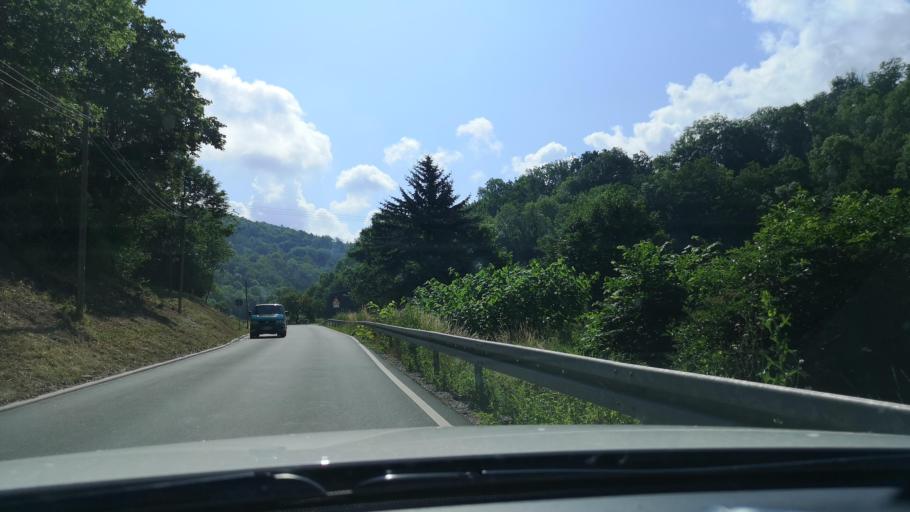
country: DE
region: Thuringia
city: Tautenburg
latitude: 51.0111
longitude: 11.7003
